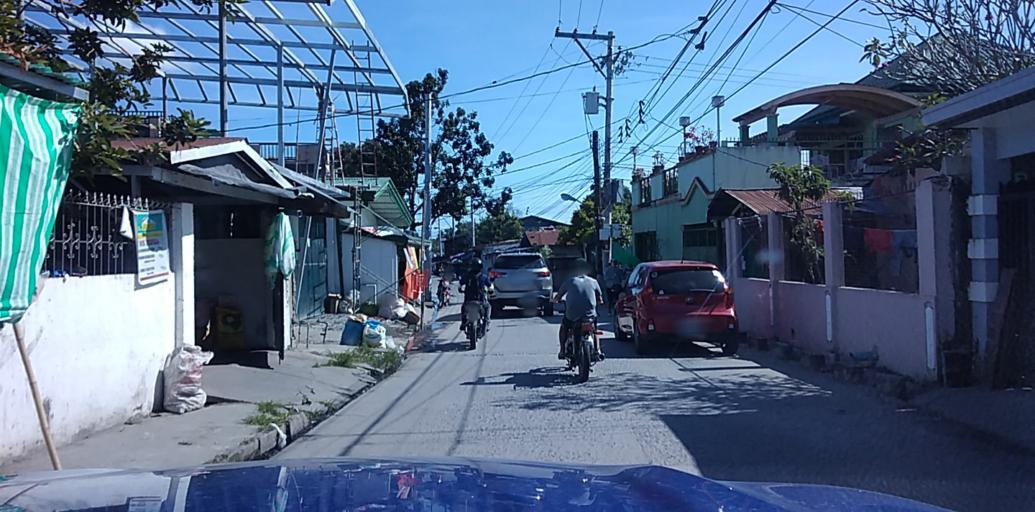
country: PH
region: Central Luzon
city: Santol
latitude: 15.1692
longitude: 120.5121
